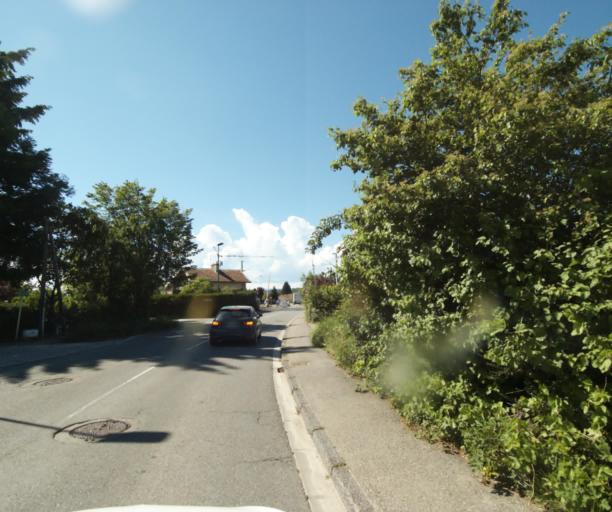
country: FR
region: Rhone-Alpes
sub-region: Departement de la Haute-Savoie
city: Bons-en-Chablais
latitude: 46.2709
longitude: 6.3624
